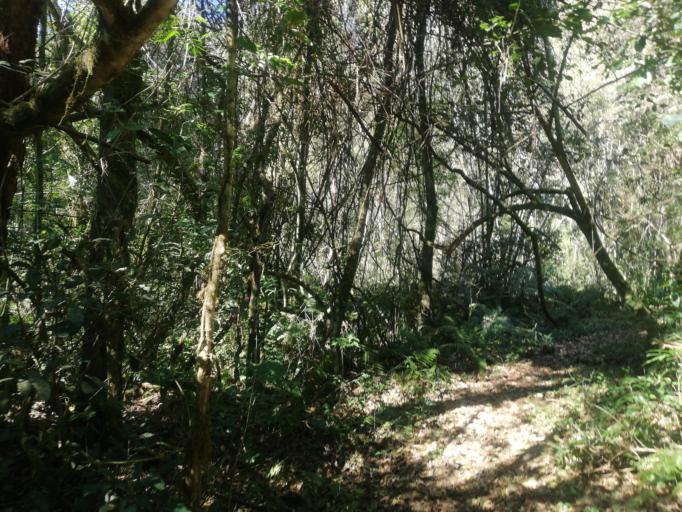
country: AR
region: Misiones
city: Colonia Wanda
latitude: -25.8598
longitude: -54.1682
